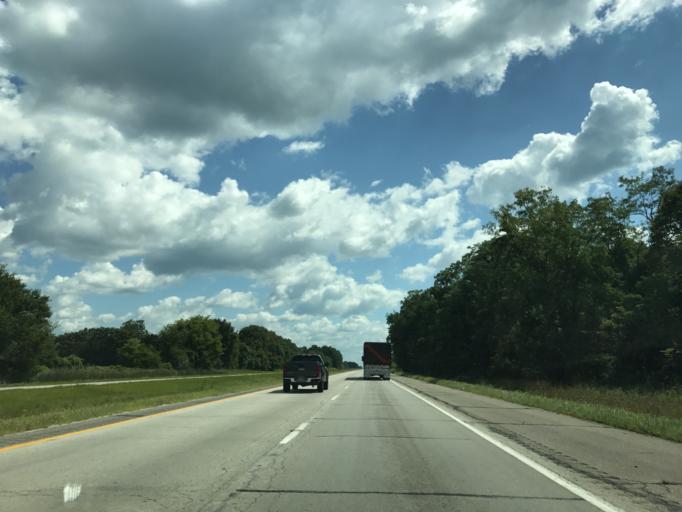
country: US
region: Indiana
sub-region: Starke County
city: Koontz Lake
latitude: 41.3644
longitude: -86.4381
